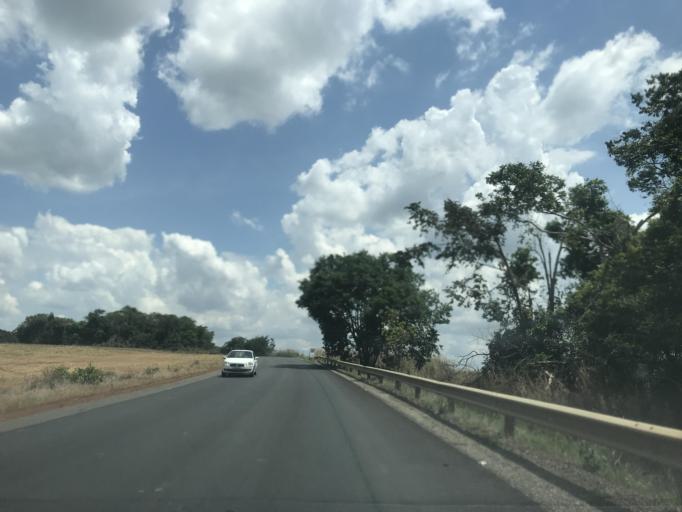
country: BR
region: Goias
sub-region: Piracanjuba
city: Piracanjuba
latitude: -17.3267
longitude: -48.8011
